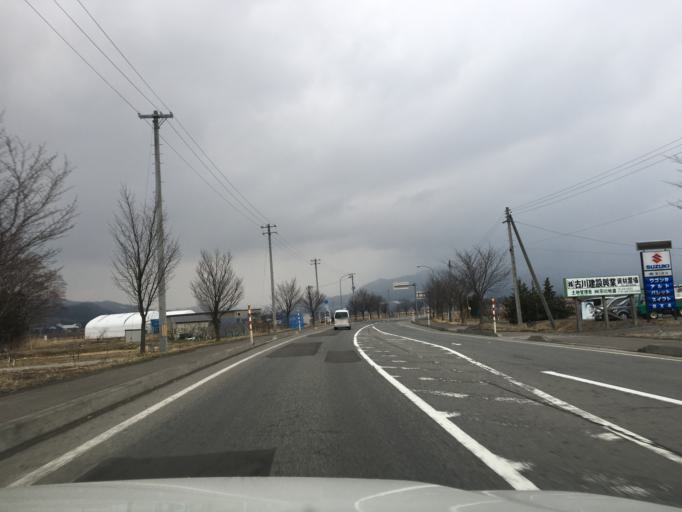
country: JP
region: Aomori
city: Kuroishi
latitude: 40.5717
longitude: 140.5678
